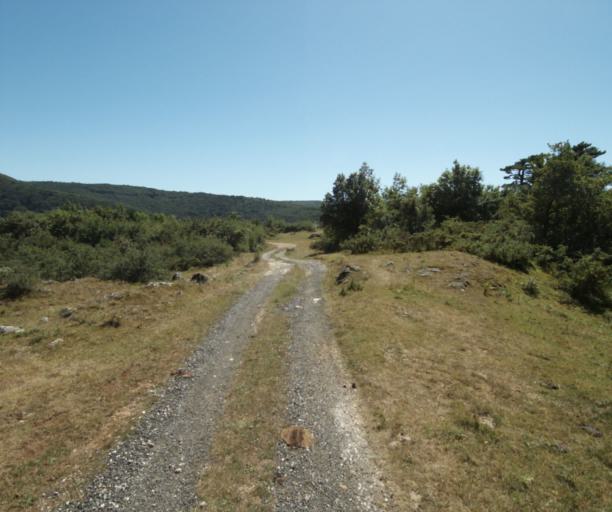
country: FR
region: Midi-Pyrenees
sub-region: Departement du Tarn
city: Soreze
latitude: 43.4459
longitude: 2.0873
